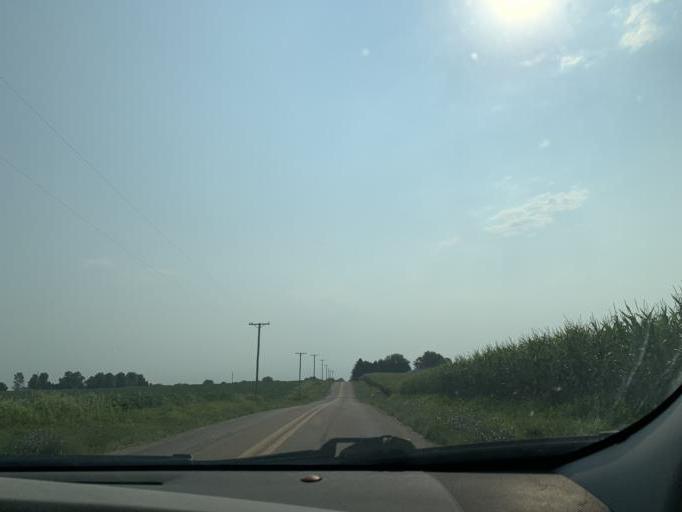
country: US
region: Illinois
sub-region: Carroll County
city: Milledgeville
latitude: 41.8479
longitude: -89.8244
